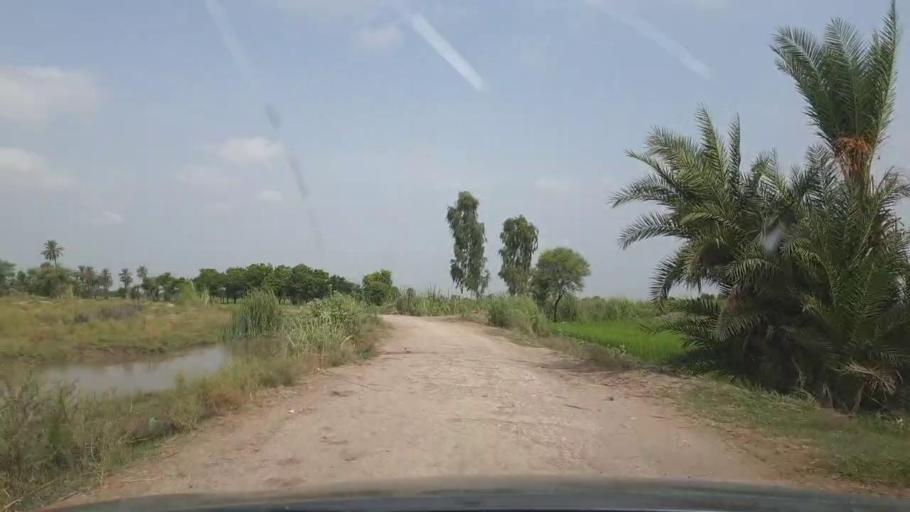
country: PK
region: Sindh
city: Ratodero
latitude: 27.8468
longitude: 68.3072
